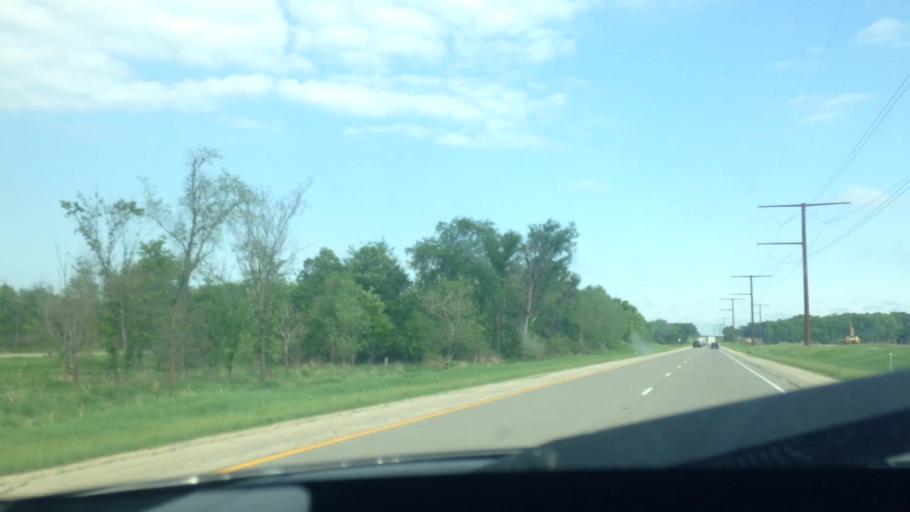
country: US
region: Wisconsin
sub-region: Juneau County
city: New Lisbon
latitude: 43.8544
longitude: -90.1077
